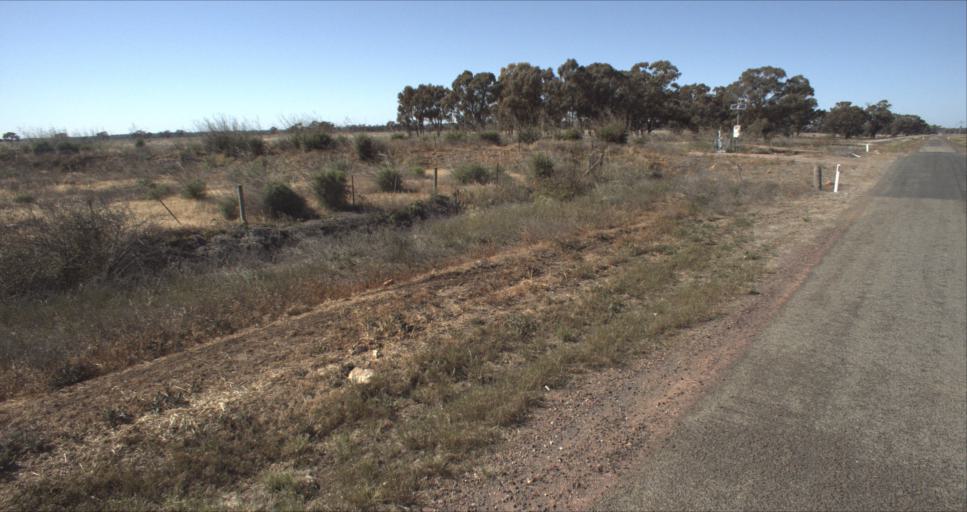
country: AU
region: New South Wales
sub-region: Leeton
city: Leeton
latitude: -34.5877
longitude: 146.2603
